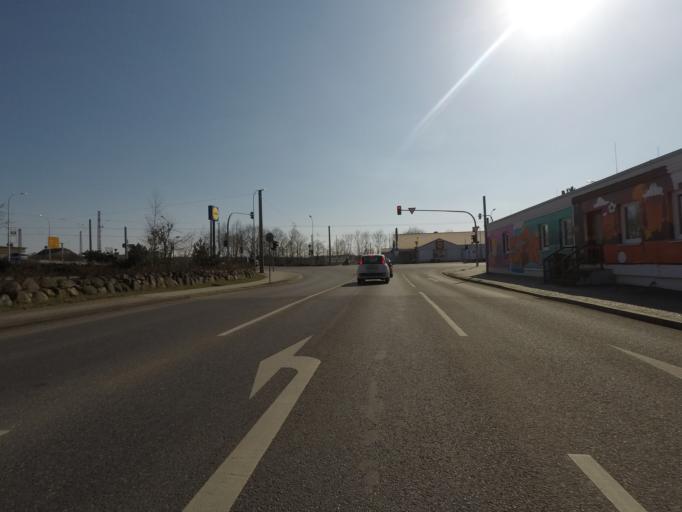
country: DE
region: Brandenburg
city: Eberswalde
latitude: 52.8355
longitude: 13.7961
